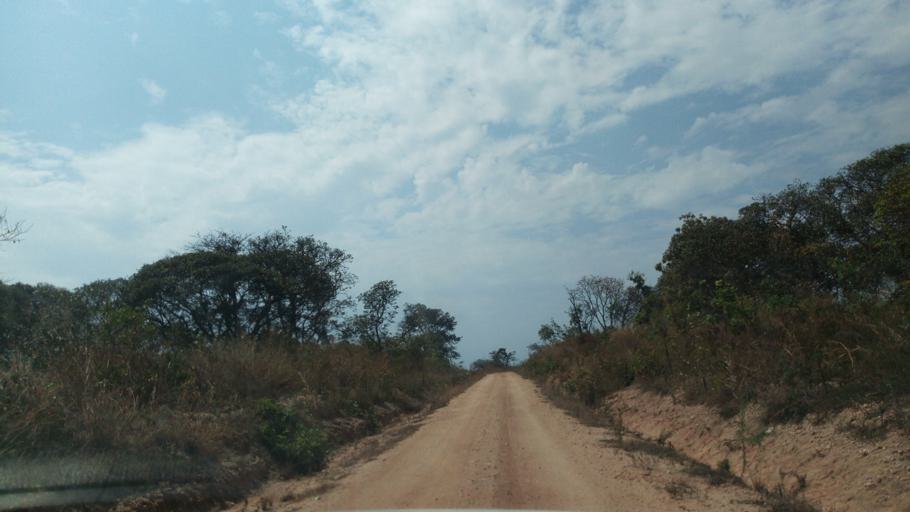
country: CD
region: Katanga
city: Kalemie
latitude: -6.2809
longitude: 29.0214
